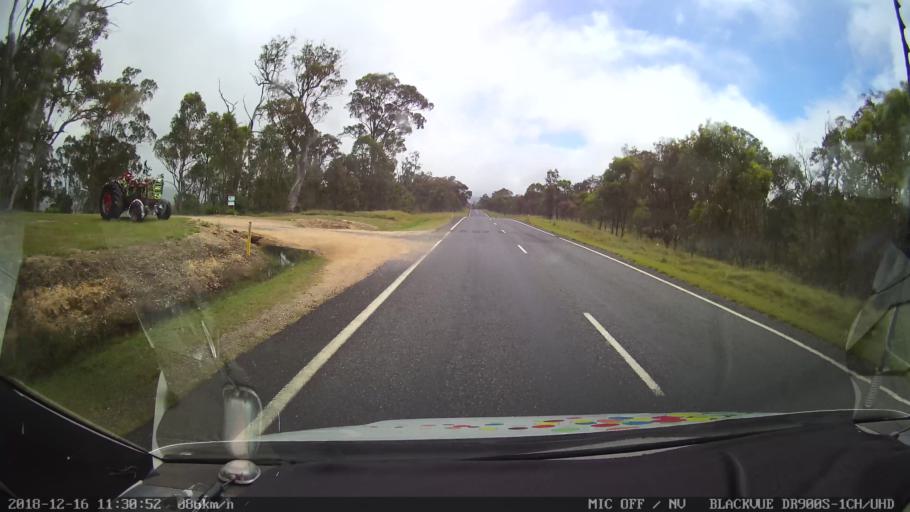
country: AU
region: New South Wales
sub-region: Tenterfield Municipality
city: Carrolls Creek
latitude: -29.0273
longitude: 152.1226
